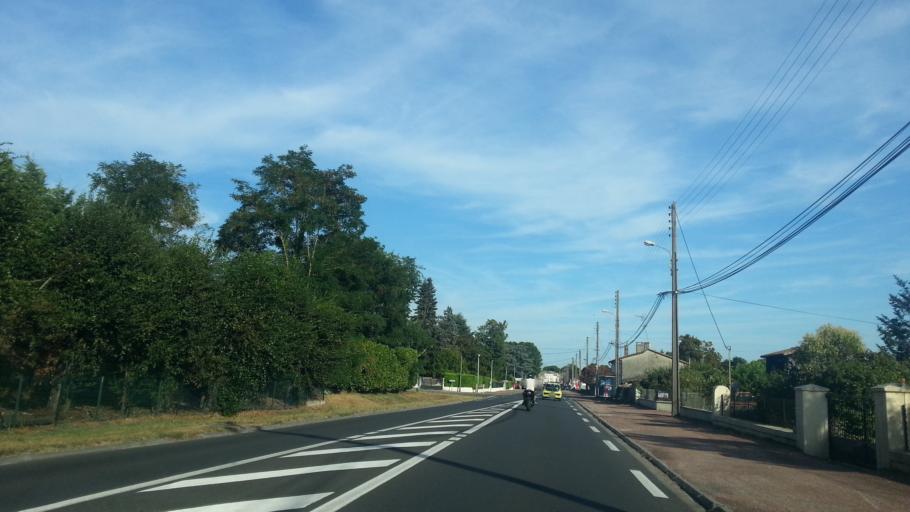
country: FR
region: Aquitaine
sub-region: Departement de la Gironde
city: Podensac
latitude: 44.6552
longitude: -0.3634
